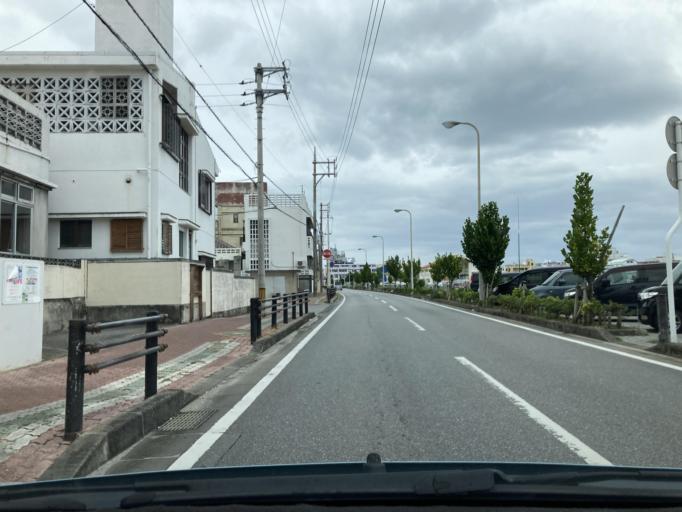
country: JP
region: Okinawa
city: Itoman
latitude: 26.1324
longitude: 127.6688
